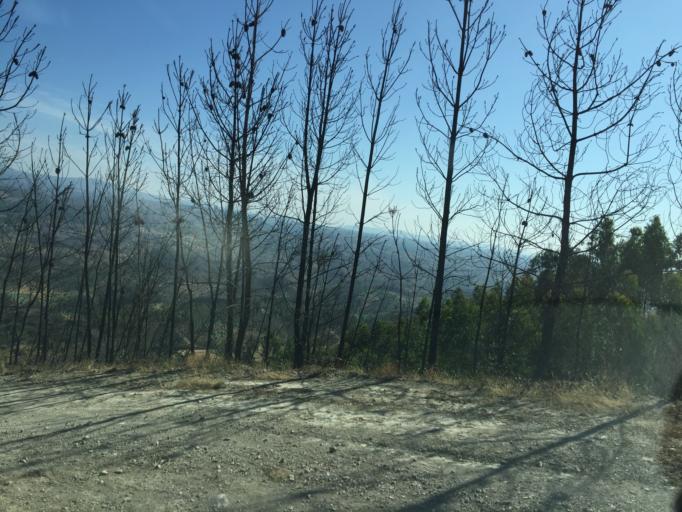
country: PT
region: Santarem
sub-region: Macao
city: Macao
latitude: 39.6559
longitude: -7.9829
